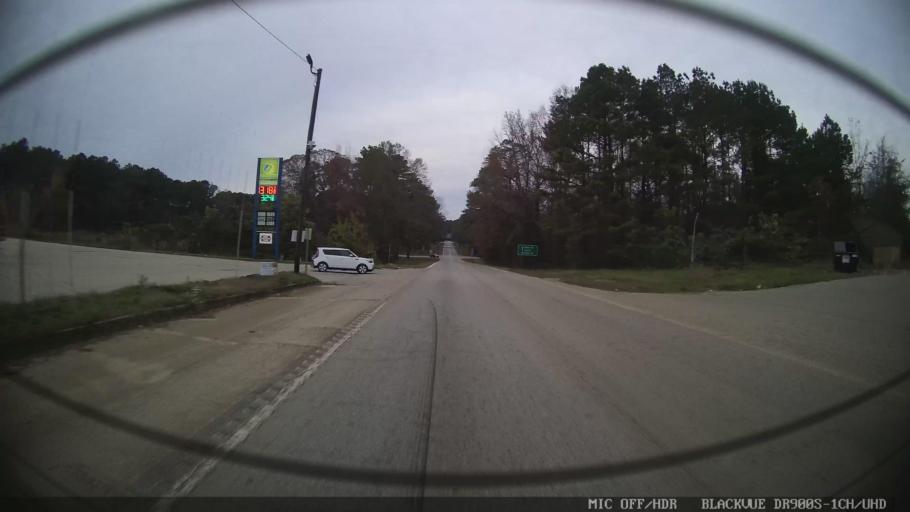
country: US
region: Mississippi
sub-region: Clarke County
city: Stonewall
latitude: 32.0580
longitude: -88.9018
